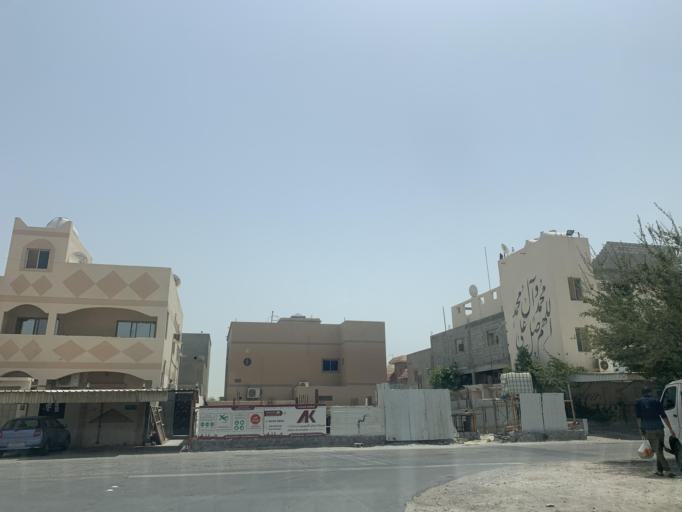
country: BH
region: Northern
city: Madinat `Isa
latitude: 26.1532
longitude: 50.5211
